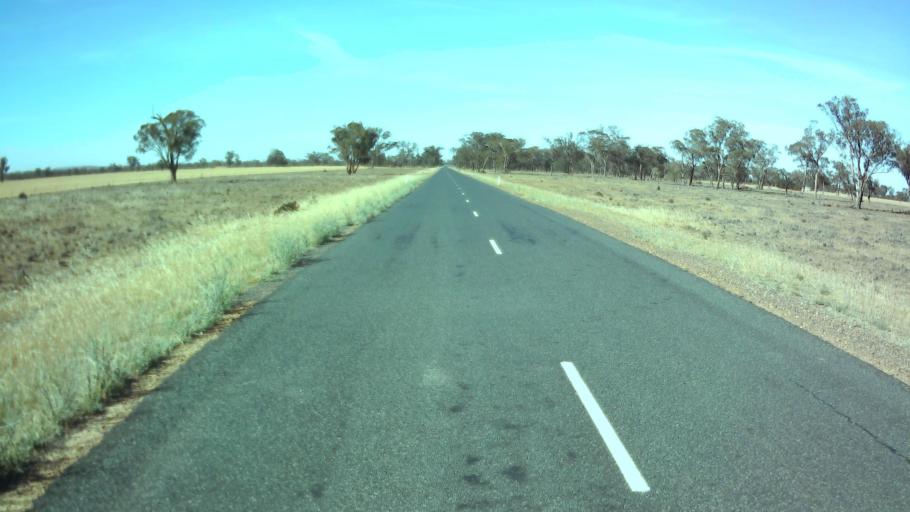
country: AU
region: New South Wales
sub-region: Weddin
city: Grenfell
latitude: -34.0854
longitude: 147.8929
